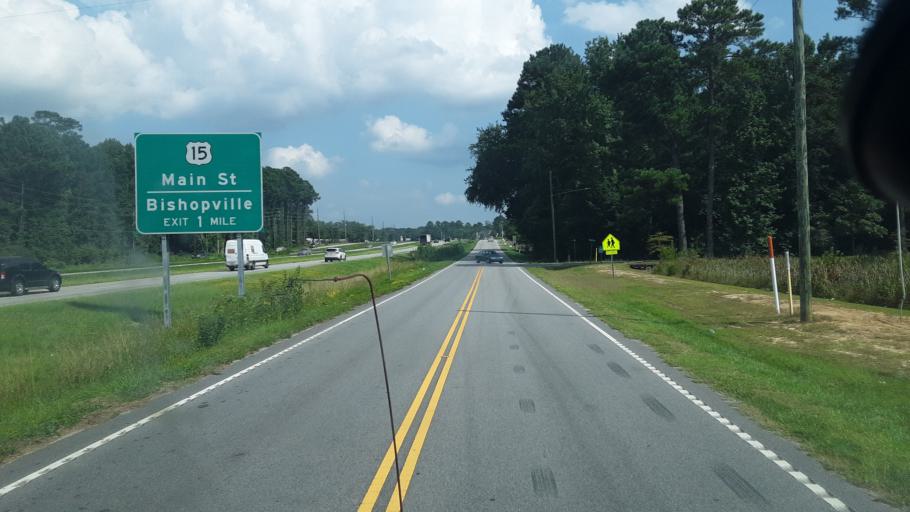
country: US
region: South Carolina
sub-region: Sumter County
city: Sumter
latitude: 33.9503
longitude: -80.3625
